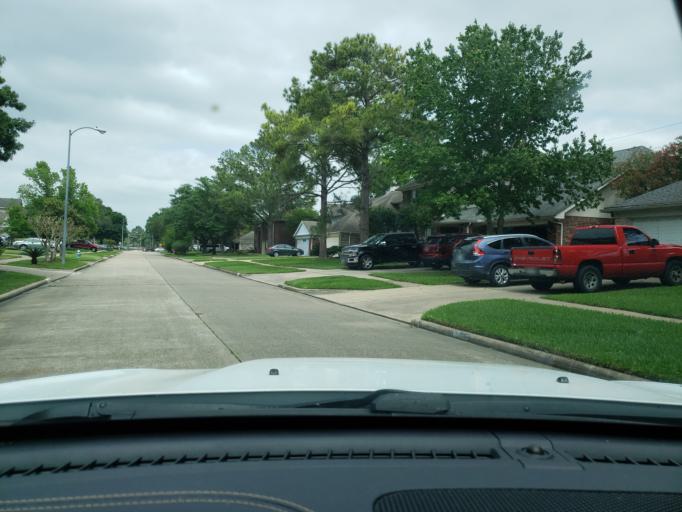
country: US
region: Texas
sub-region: Harris County
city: Jersey Village
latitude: 29.9198
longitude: -95.5718
